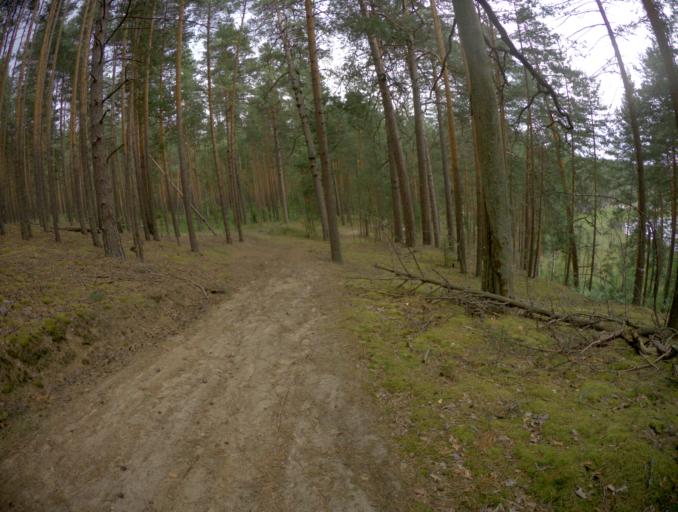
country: RU
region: Nizjnij Novgorod
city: Frolishchi
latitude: 56.3551
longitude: 42.7402
